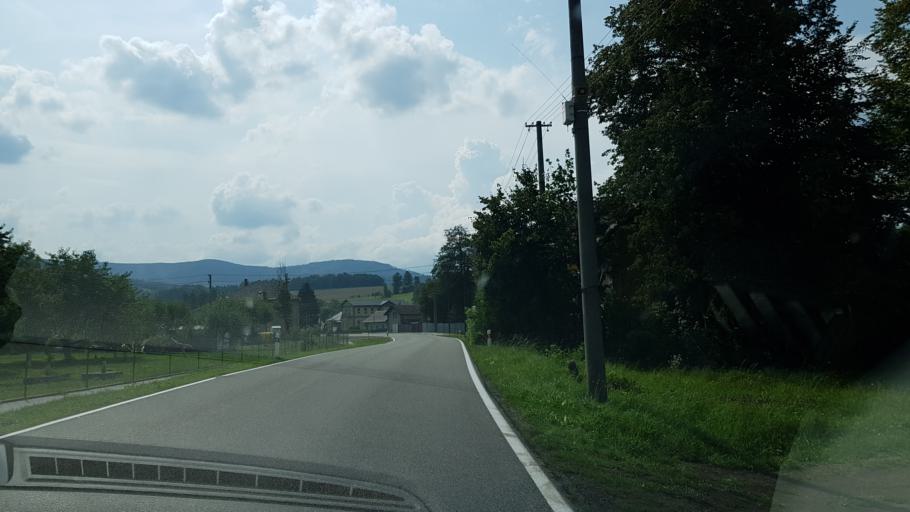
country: CZ
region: Olomoucky
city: Pisecna
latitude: 50.2773
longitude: 17.2812
